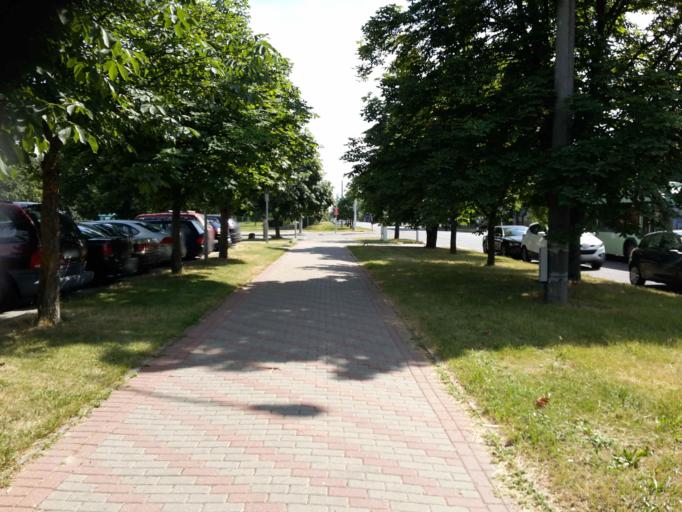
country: BY
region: Minsk
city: Minsk
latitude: 53.9400
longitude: 27.5662
